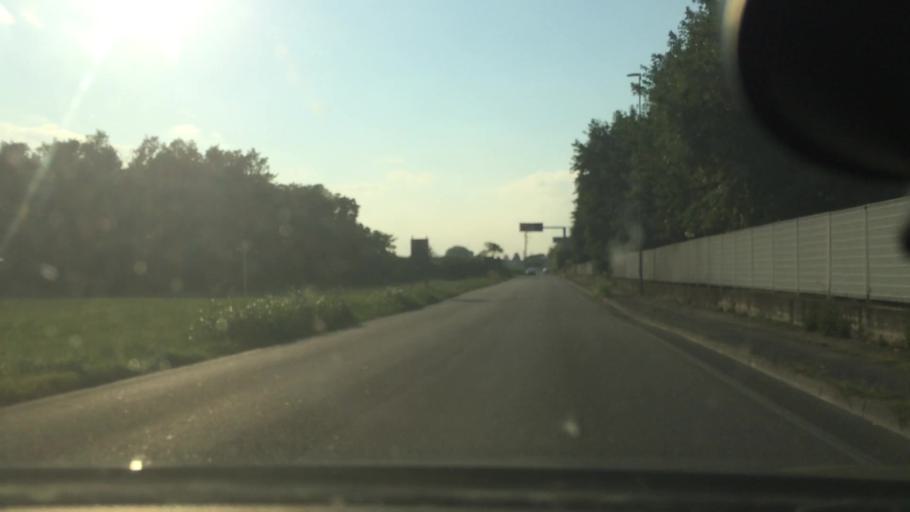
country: IT
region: Lombardy
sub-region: Citta metropolitana di Milano
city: Pogliano Milanese
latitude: 45.5356
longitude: 9.0122
